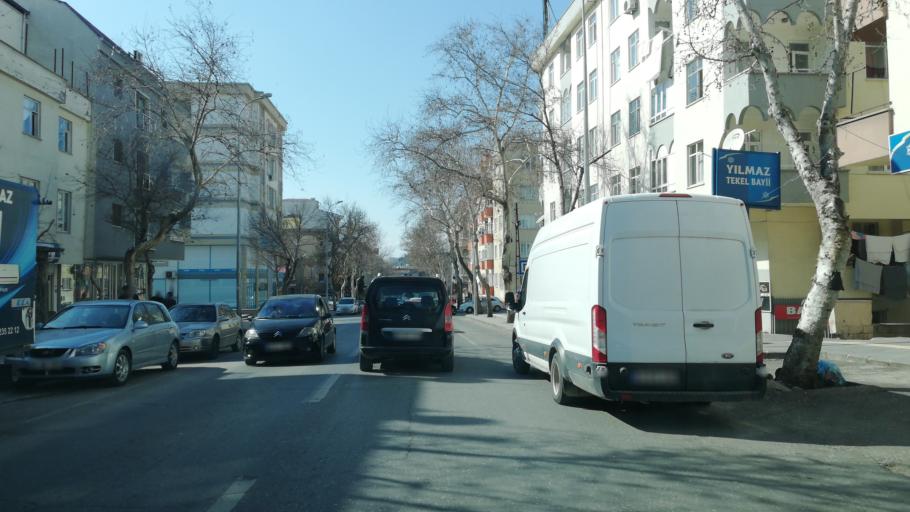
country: TR
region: Kahramanmaras
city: Kahramanmaras
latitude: 37.5720
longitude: 36.9305
